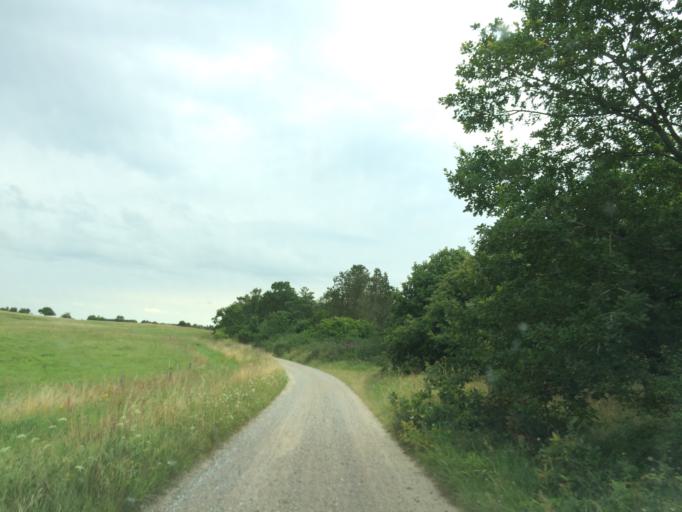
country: DK
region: Central Jutland
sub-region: Syddjurs Kommune
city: Ronde
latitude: 56.2277
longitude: 10.5421
